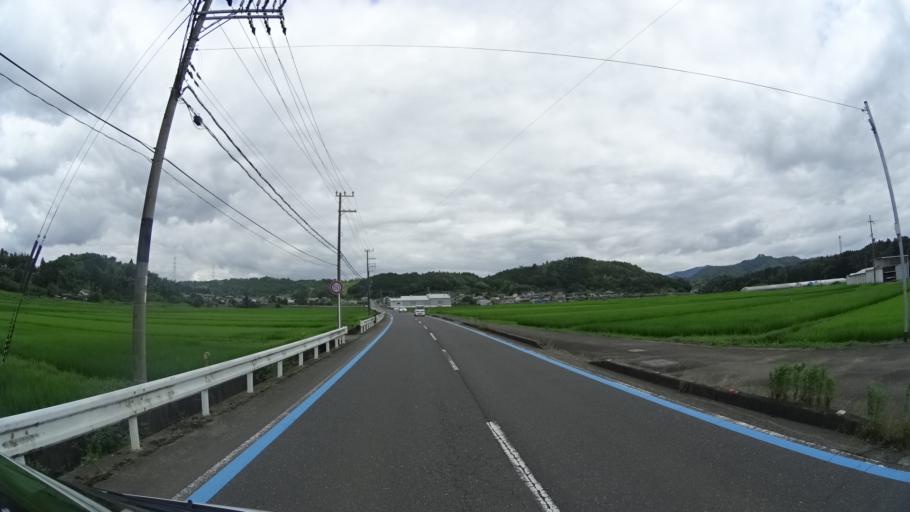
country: JP
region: Kyoto
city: Ayabe
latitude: 35.3186
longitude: 135.2649
